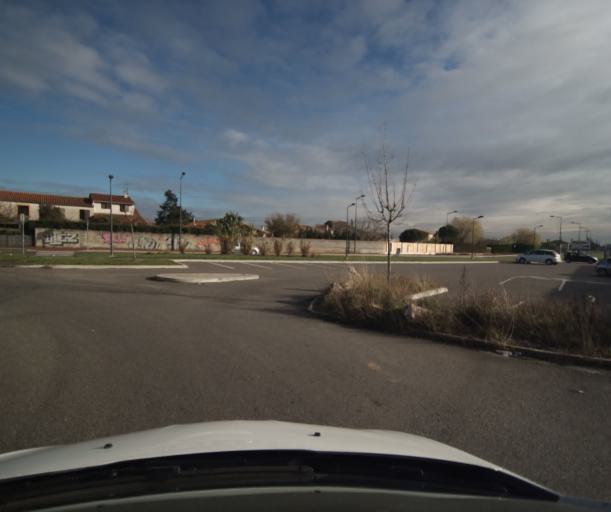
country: FR
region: Midi-Pyrenees
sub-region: Departement de la Haute-Garonne
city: Bruguieres
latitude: 43.7203
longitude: 1.4153
